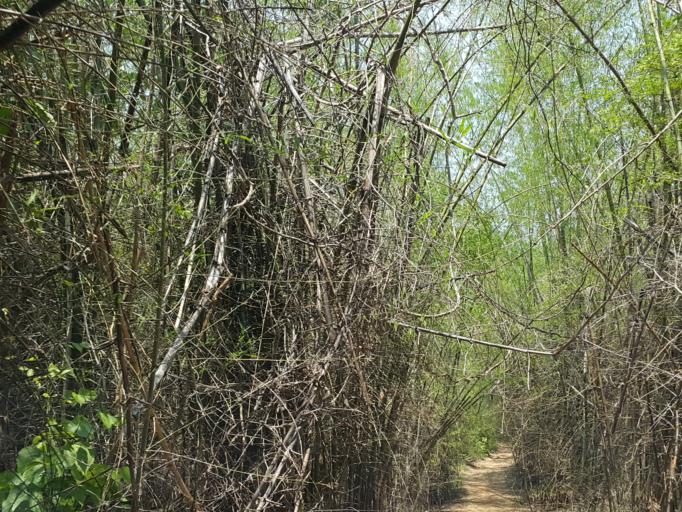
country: TH
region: Kanchanaburi
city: Sai Yok
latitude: 14.2126
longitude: 98.8789
